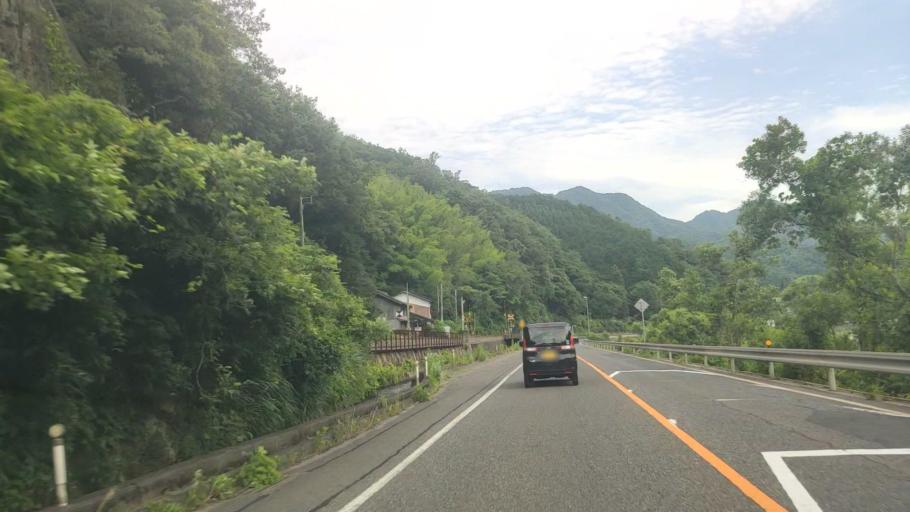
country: JP
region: Tottori
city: Tottori
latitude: 35.3498
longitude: 134.2046
